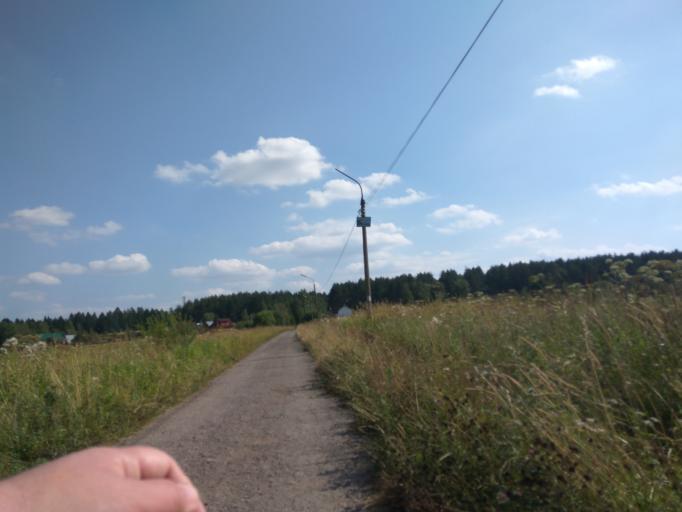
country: RU
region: Moskovskaya
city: Kubinka
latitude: 55.5848
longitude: 36.7587
